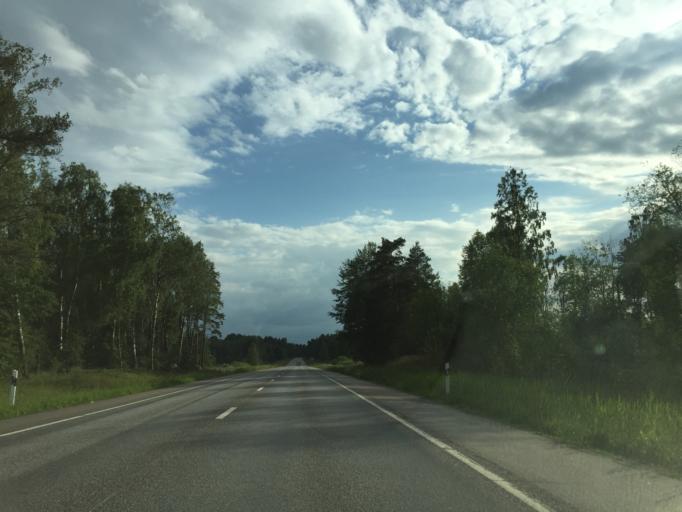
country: SE
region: OErebro
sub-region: Lindesbergs Kommun
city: Fellingsbro
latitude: 59.3610
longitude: 15.6897
